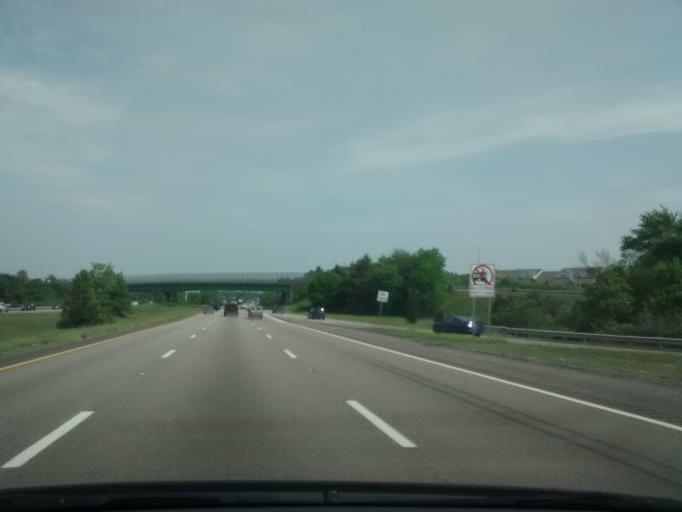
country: US
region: Massachusetts
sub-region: Bristol County
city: Mansfield
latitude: 42.0252
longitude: -71.2546
